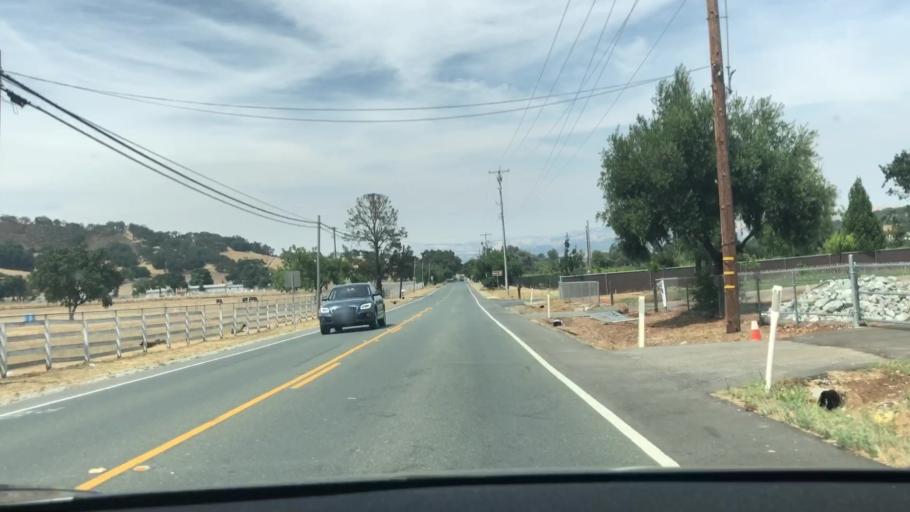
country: US
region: California
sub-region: Santa Clara County
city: San Martin
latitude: 37.0721
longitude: -121.6585
